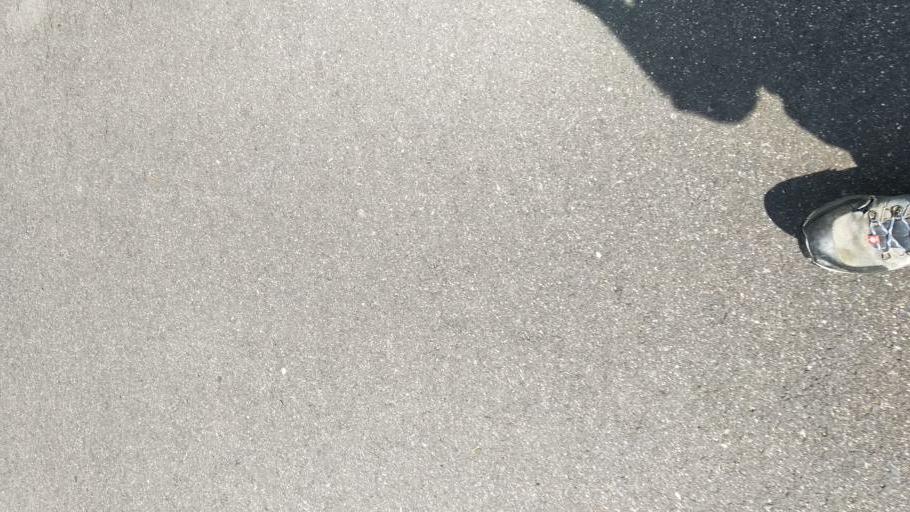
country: DE
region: North Rhine-Westphalia
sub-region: Regierungsbezirk Dusseldorf
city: Monchengladbach
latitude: 51.1748
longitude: 6.3888
